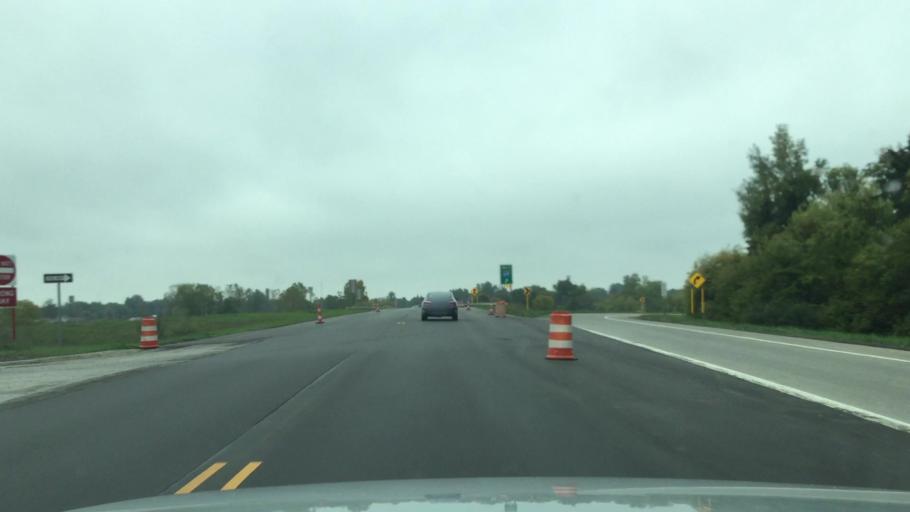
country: US
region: Michigan
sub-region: Shiawassee County
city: Perry
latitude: 42.8422
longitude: -84.2199
